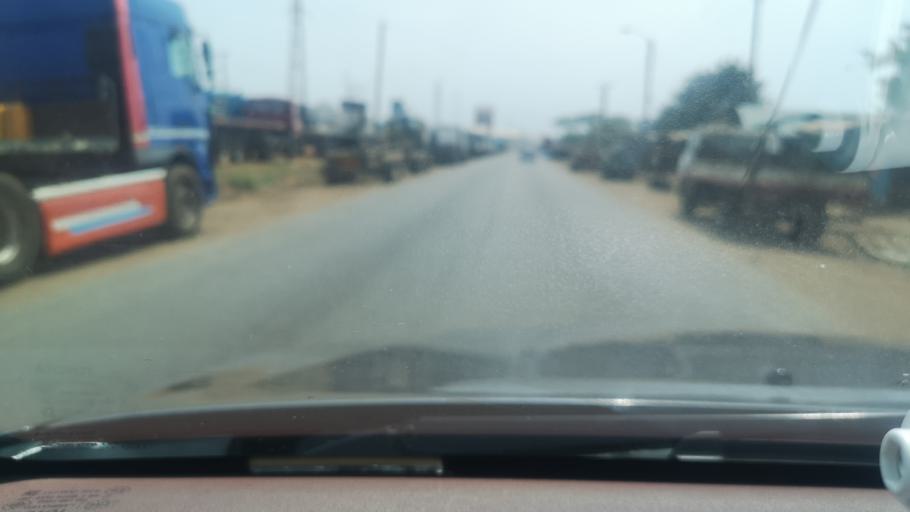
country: GH
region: Greater Accra
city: Tema
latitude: 5.6278
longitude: -0.0113
